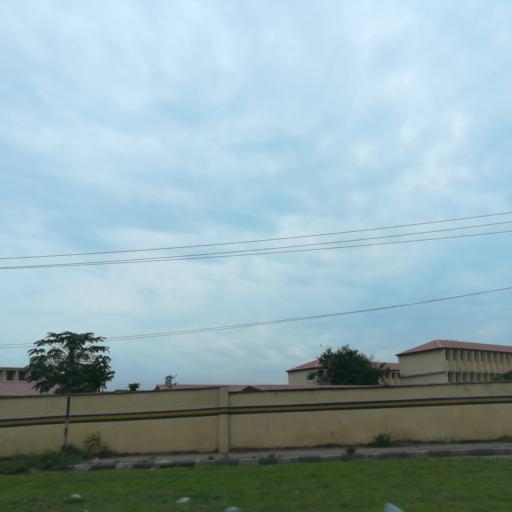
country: NG
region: Lagos
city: Ikeja
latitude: 6.5917
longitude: 3.3487
